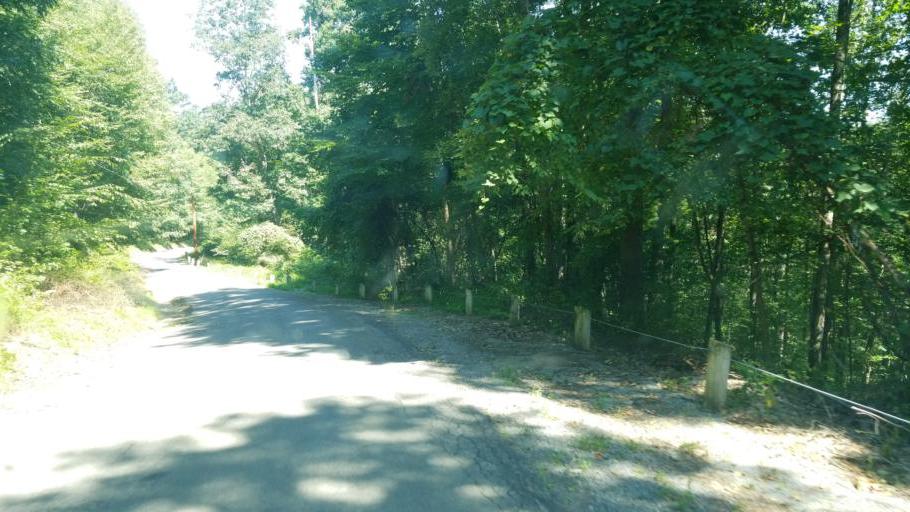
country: US
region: Pennsylvania
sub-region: Clarion County
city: Clarion
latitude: 41.1852
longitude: -79.4333
